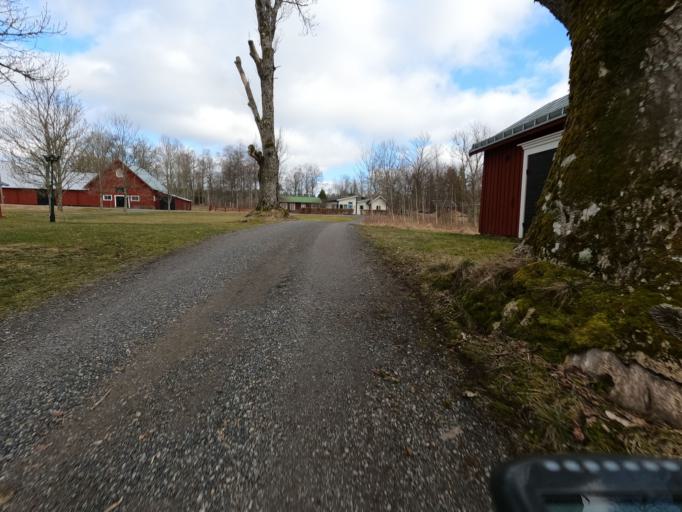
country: SE
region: Kronoberg
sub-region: Alvesta Kommun
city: Vislanda
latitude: 56.8167
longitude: 14.3726
